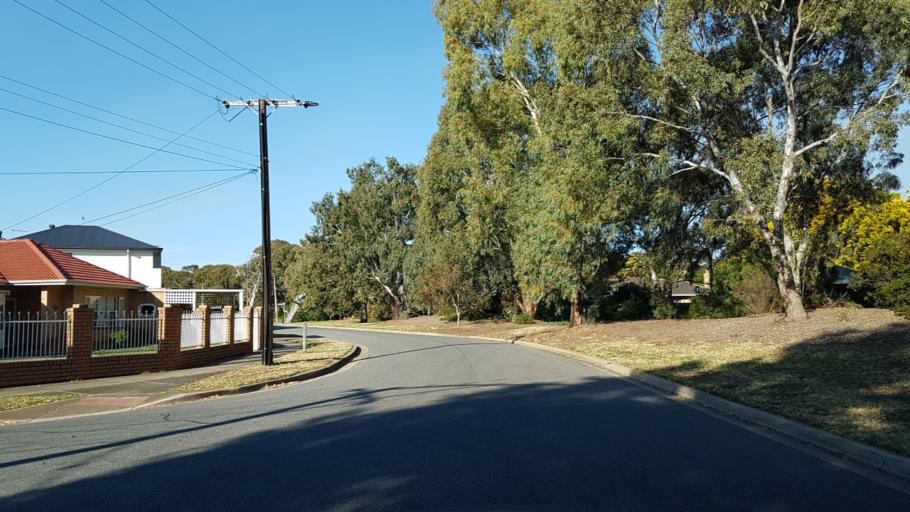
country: AU
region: South Australia
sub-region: Charles Sturt
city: Seaton
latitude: -34.9237
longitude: 138.5184
